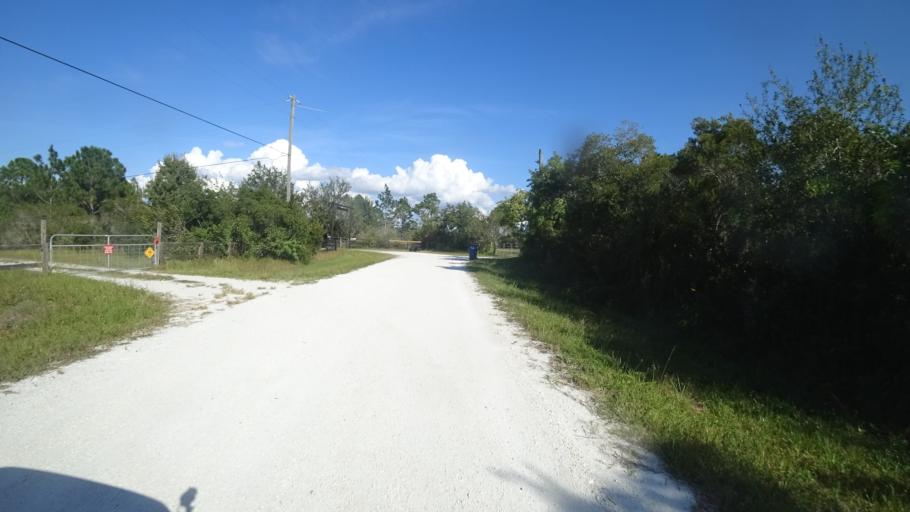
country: US
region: Florida
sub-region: Sarasota County
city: Lake Sarasota
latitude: 27.3940
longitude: -82.2899
